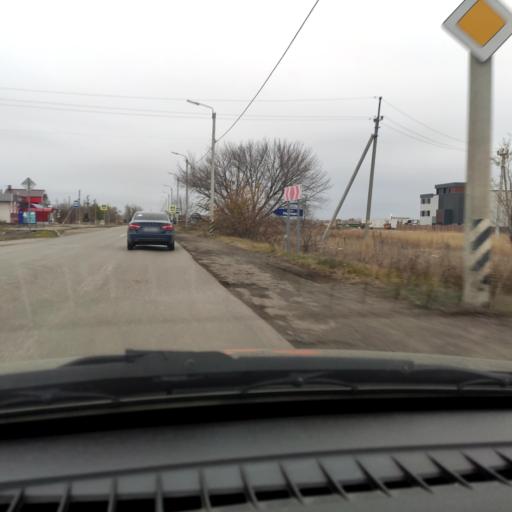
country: RU
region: Samara
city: Podstepki
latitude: 53.5220
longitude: 49.1803
